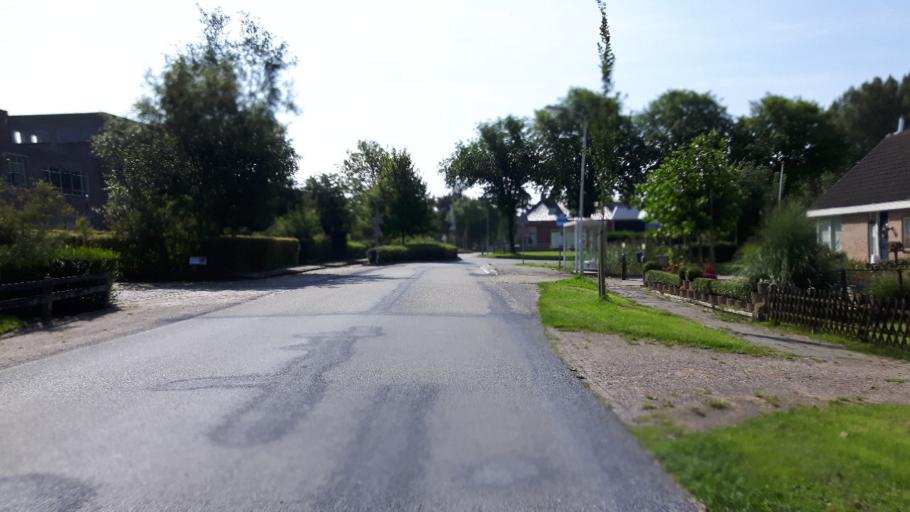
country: NL
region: Friesland
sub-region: Gemeente Ferwerderadiel
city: Marrum
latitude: 53.3265
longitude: 5.8034
